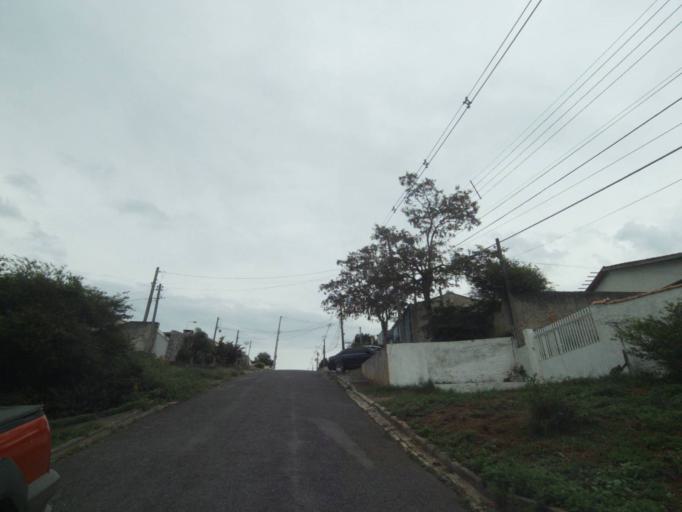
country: BR
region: Parana
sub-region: Curitiba
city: Curitiba
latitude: -25.4001
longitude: -49.3023
